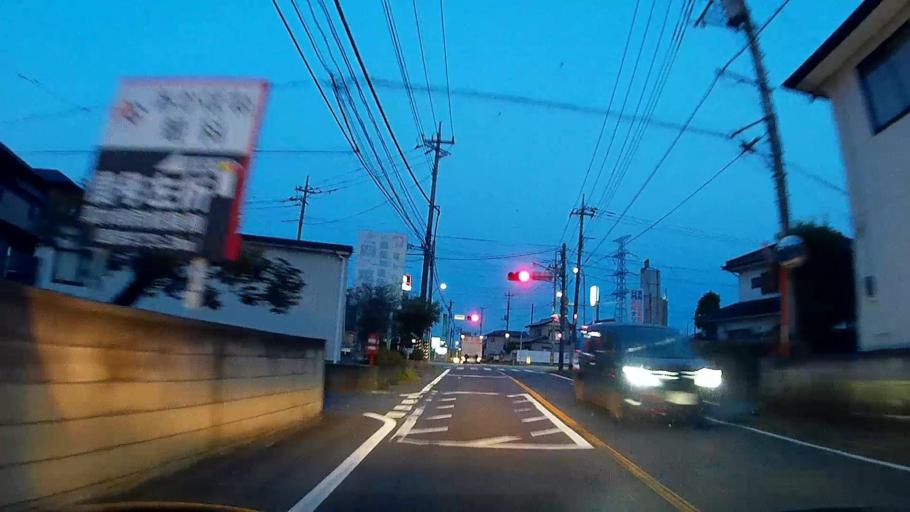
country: JP
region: Gunma
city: Takasaki
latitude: 36.3435
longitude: 138.9651
